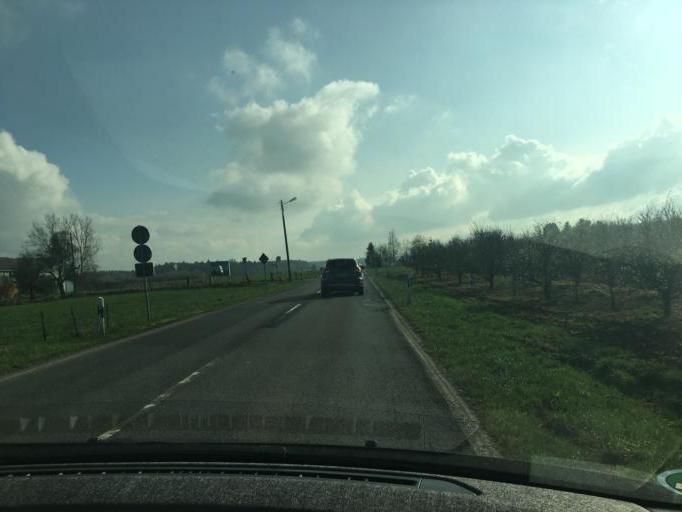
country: DE
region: North Rhine-Westphalia
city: Bornheim
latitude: 50.7421
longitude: 6.9565
